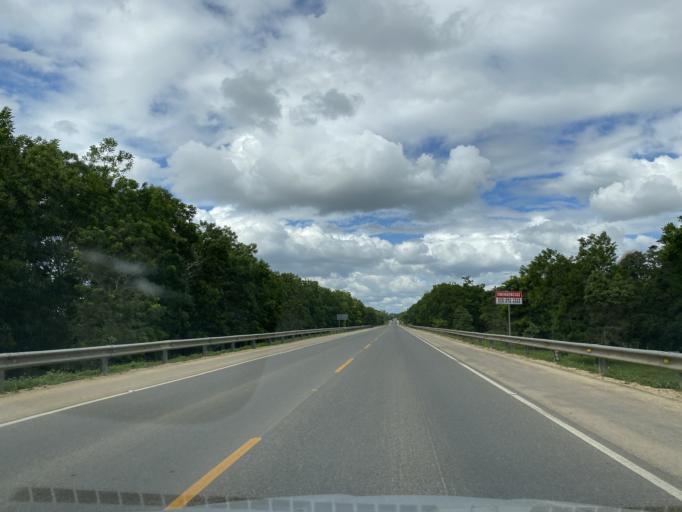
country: DO
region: Santo Domingo
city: Guerra
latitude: 18.5385
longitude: -69.7564
